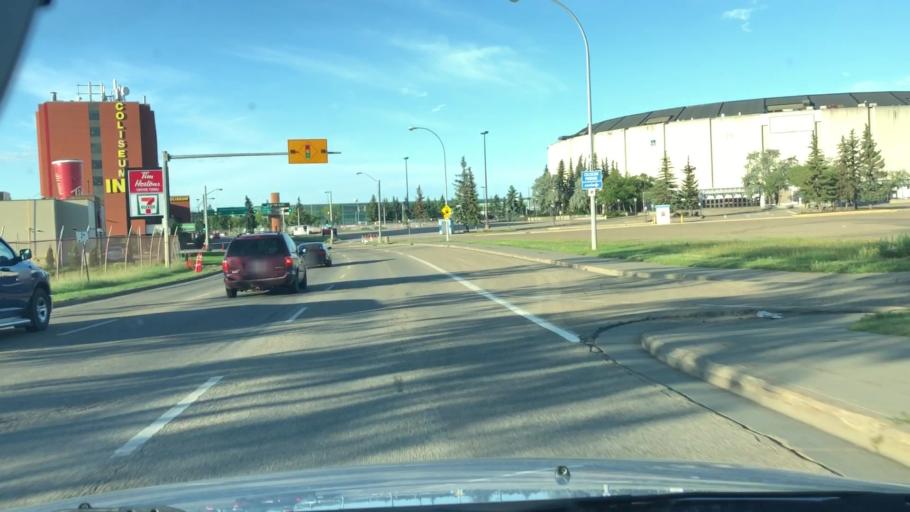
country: CA
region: Alberta
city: Edmonton
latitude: 53.5731
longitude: -113.4535
